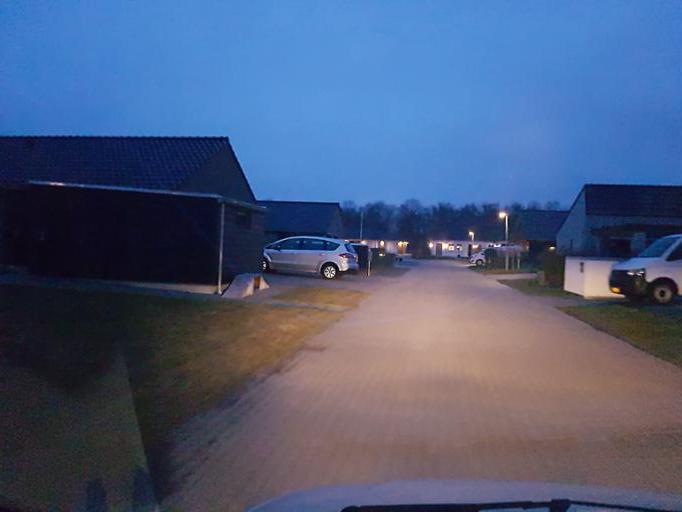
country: DK
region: South Denmark
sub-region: Esbjerg Kommune
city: Bramming
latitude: 55.4748
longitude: 8.6849
